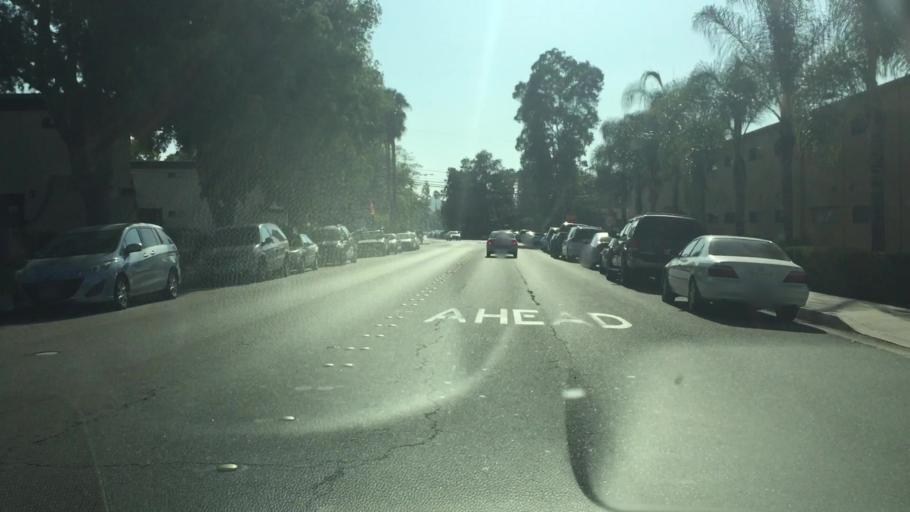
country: US
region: California
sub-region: San Diego County
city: El Cajon
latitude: 32.7929
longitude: -116.9472
